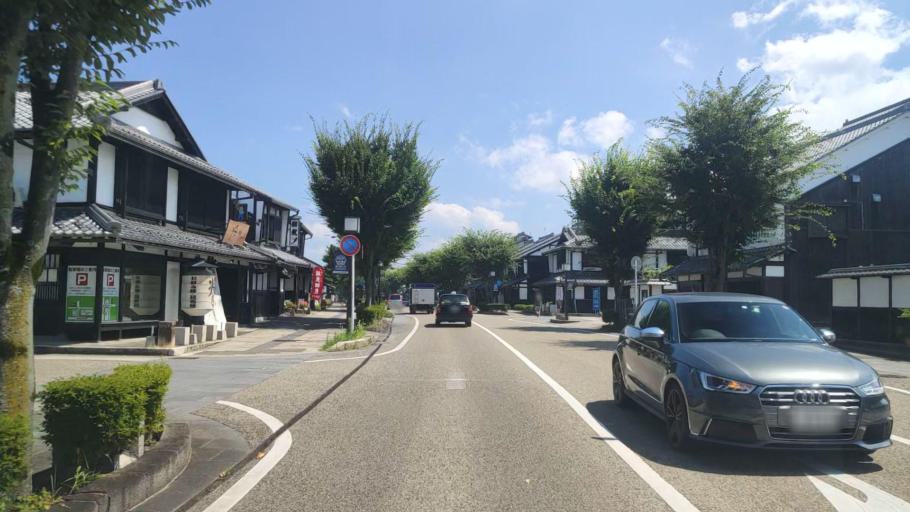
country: JP
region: Shiga Prefecture
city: Hikone
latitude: 35.2698
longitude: 136.2505
